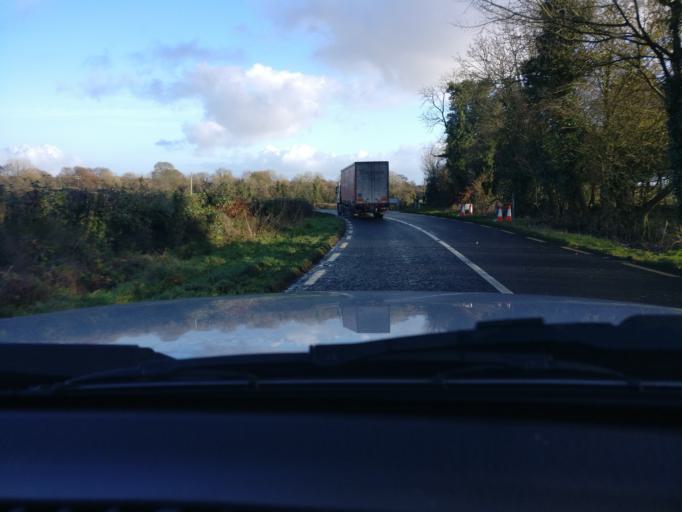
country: IE
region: Leinster
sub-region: An Iarmhi
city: Rathwire
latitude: 53.6246
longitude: -7.0664
